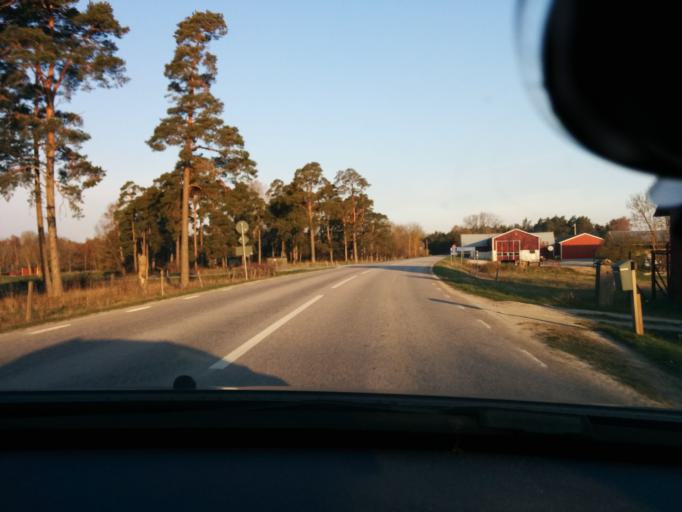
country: SE
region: Gotland
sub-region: Gotland
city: Slite
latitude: 57.6286
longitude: 18.5761
